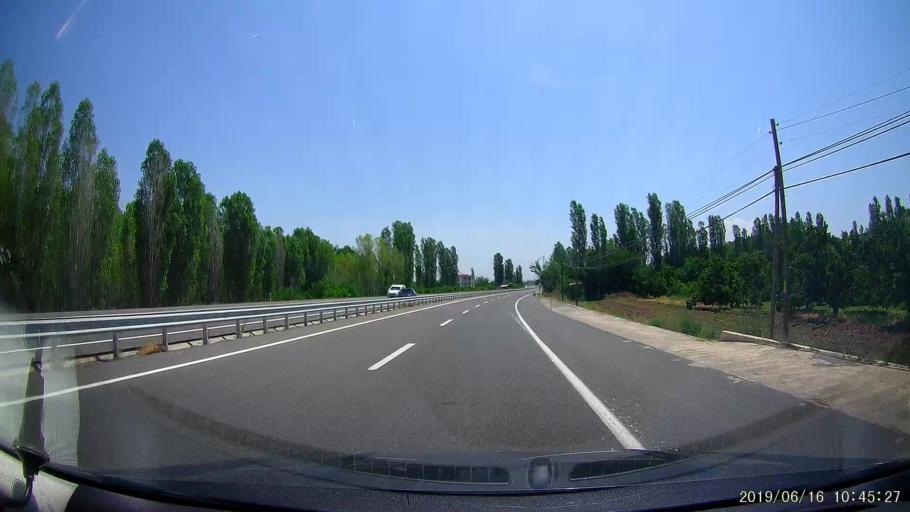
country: AM
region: Armavir
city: Shenavan
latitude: 40.0275
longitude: 43.8693
